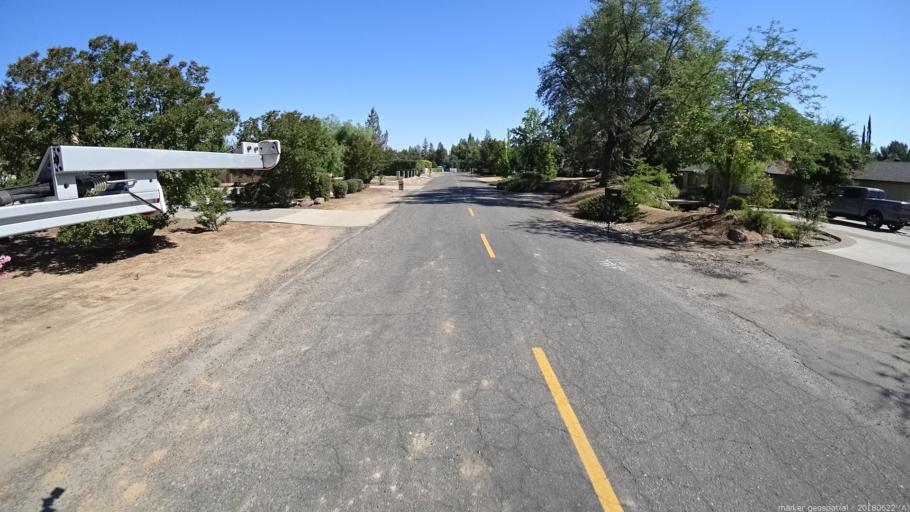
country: US
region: California
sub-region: Madera County
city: Bonadelle Ranchos-Madera Ranchos
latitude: 36.9063
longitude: -119.7972
